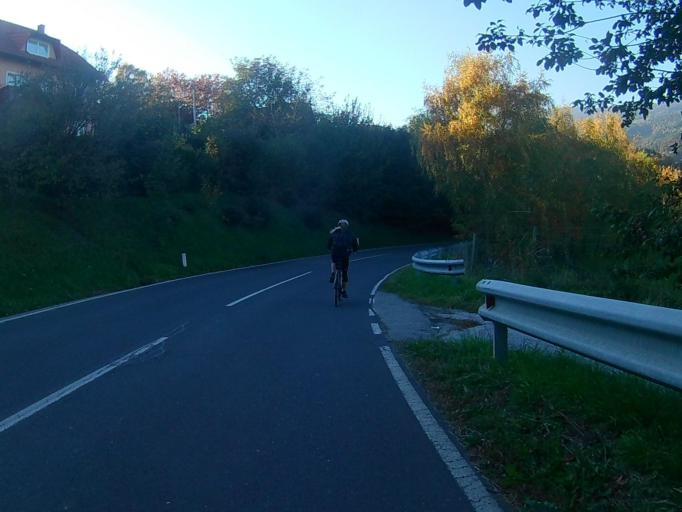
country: SI
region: Race-Fram
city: Fram
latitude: 46.4857
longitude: 15.6124
